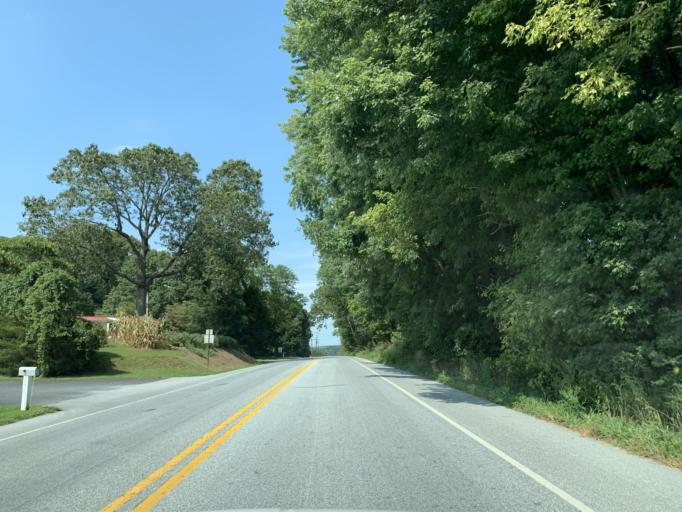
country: US
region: Pennsylvania
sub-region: York County
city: Susquehanna Trails
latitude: 39.7505
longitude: -76.3305
